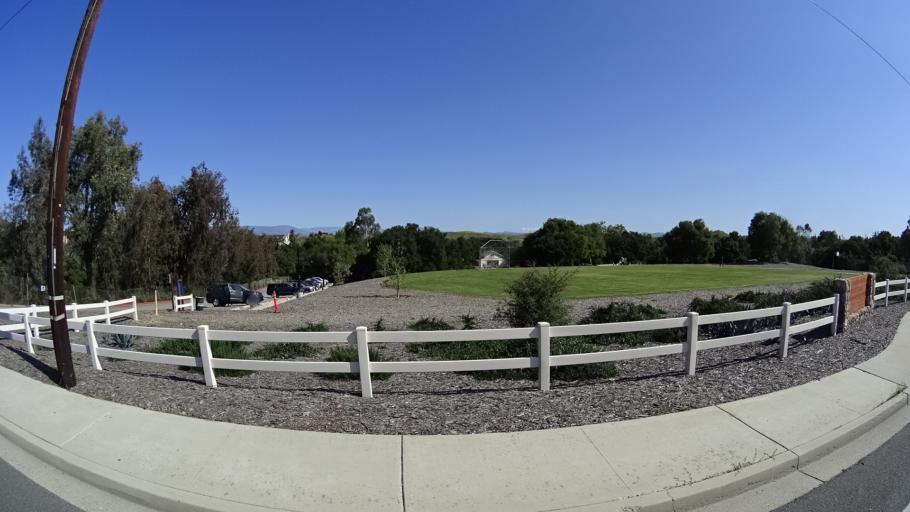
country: US
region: California
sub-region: Ventura County
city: Casa Conejo
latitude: 34.1767
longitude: -118.9127
